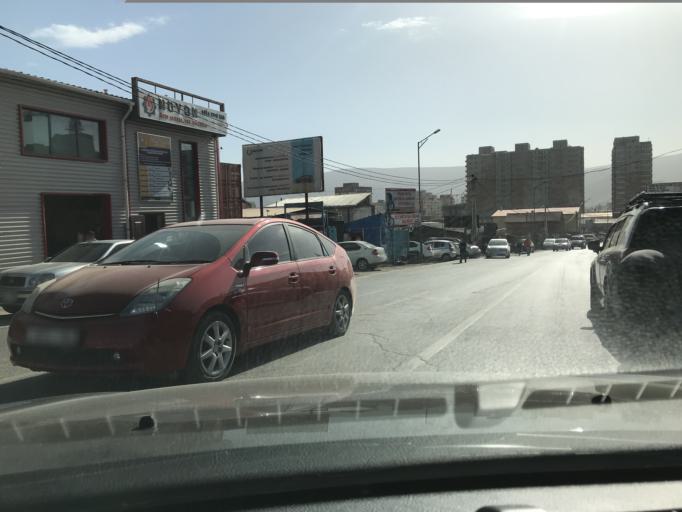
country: MN
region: Ulaanbaatar
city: Ulaanbaatar
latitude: 47.9234
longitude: 106.9612
